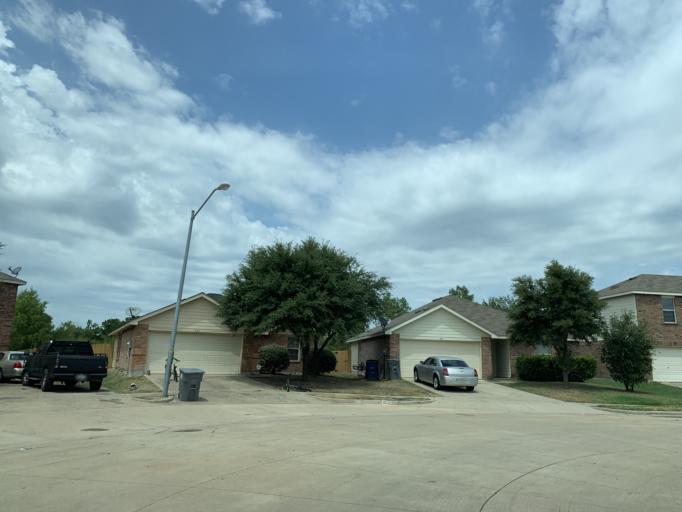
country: US
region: Texas
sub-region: Dallas County
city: DeSoto
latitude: 32.6584
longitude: -96.8153
